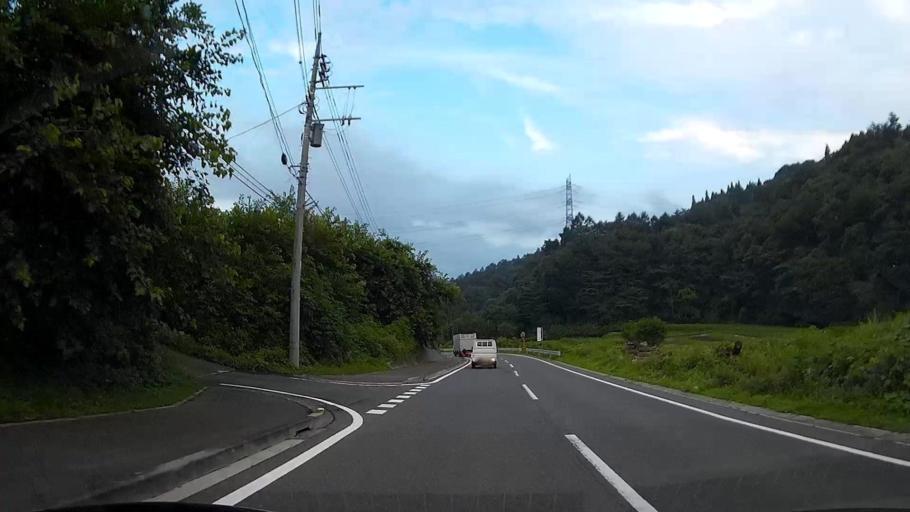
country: JP
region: Gunma
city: Nakanojomachi
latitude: 36.5273
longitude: 138.7365
